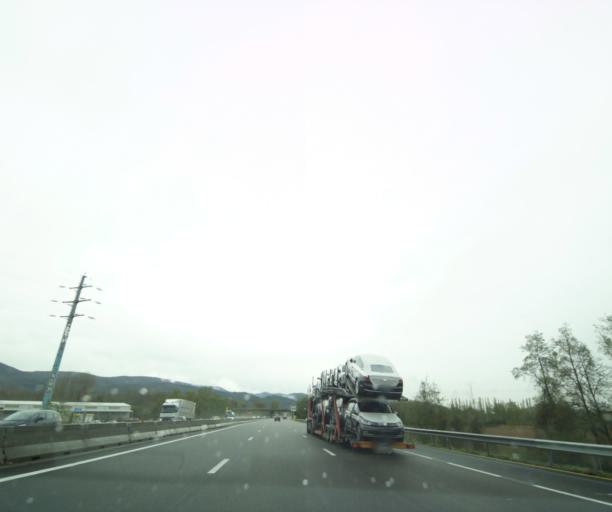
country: FR
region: Rhone-Alpes
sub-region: Departement de la Drome
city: Saulce-sur-Rhone
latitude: 44.6868
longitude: 4.7927
